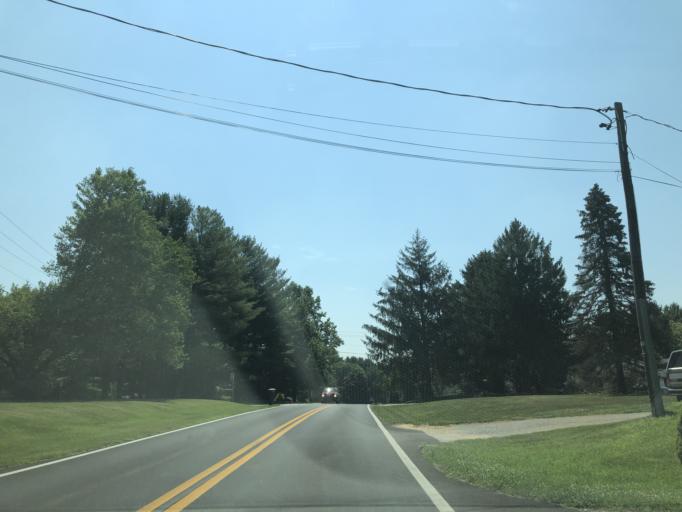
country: US
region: Maryland
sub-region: Carroll County
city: Eldersburg
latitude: 39.4428
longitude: -76.9572
